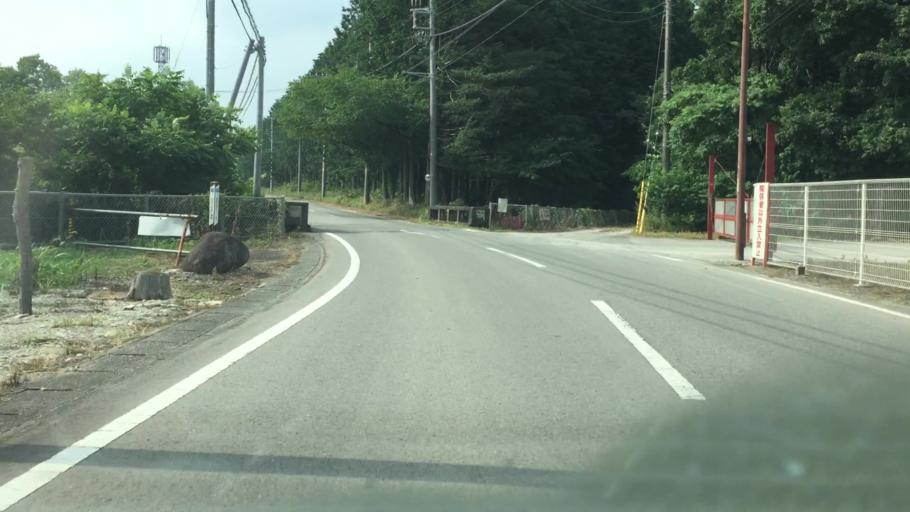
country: JP
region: Tochigi
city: Kuroiso
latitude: 36.9513
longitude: 139.9604
